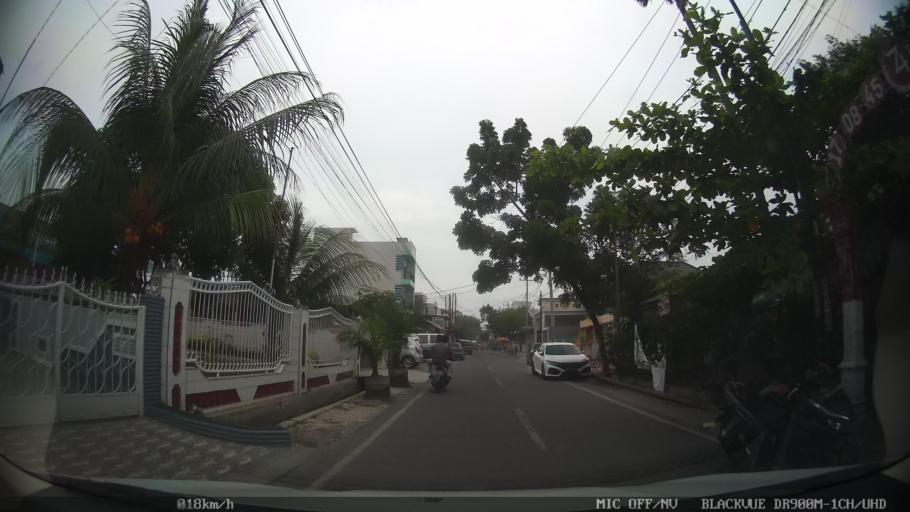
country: ID
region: North Sumatra
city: Medan
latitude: 3.5758
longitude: 98.7018
